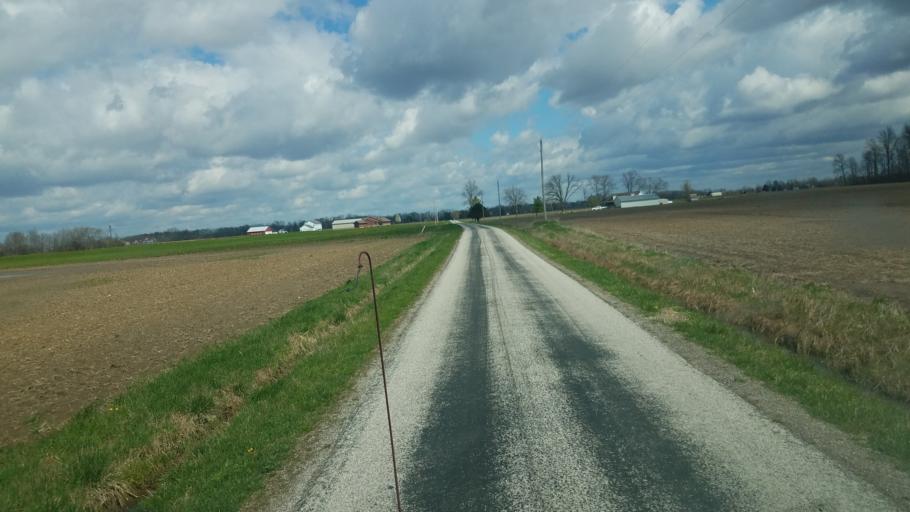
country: US
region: Ohio
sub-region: Union County
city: Richwood
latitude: 40.3533
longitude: -83.2376
